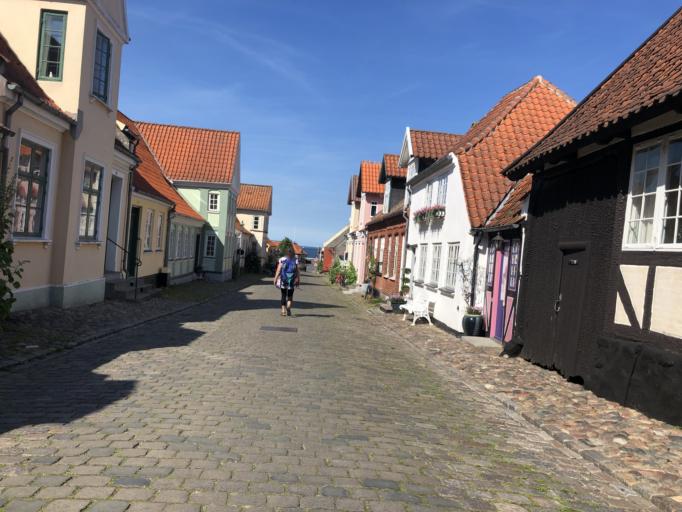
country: DK
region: South Denmark
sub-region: AEro Kommune
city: AEroskobing
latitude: 54.8898
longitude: 10.4106
